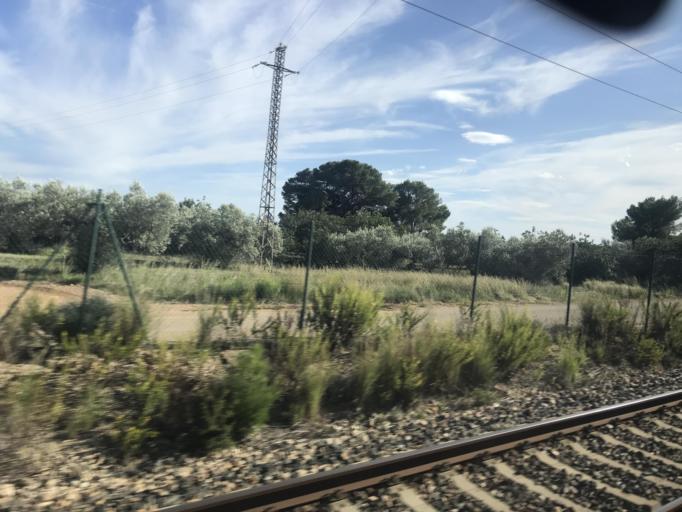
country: ES
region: Catalonia
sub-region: Provincia de Tarragona
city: l'Ametlla de Mar
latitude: 40.8614
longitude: 0.7726
